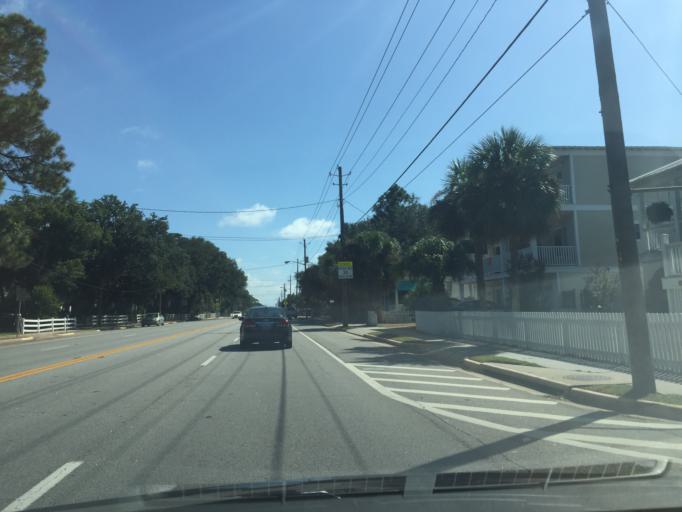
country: US
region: Georgia
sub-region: Chatham County
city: Tybee Island
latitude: 32.0051
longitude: -80.8442
